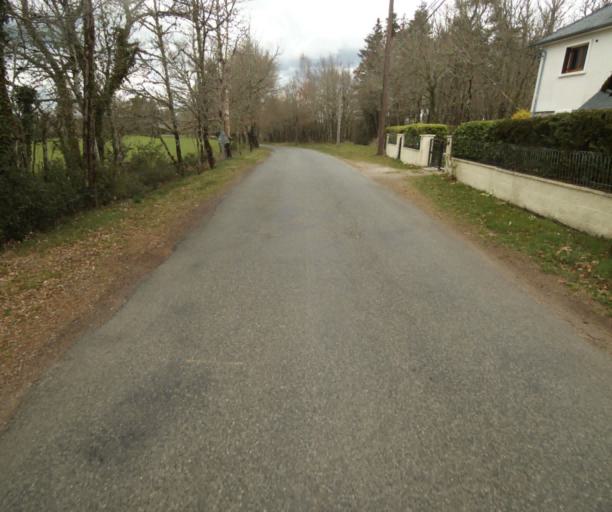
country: FR
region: Limousin
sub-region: Departement de la Correze
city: Correze
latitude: 45.3285
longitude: 1.9381
